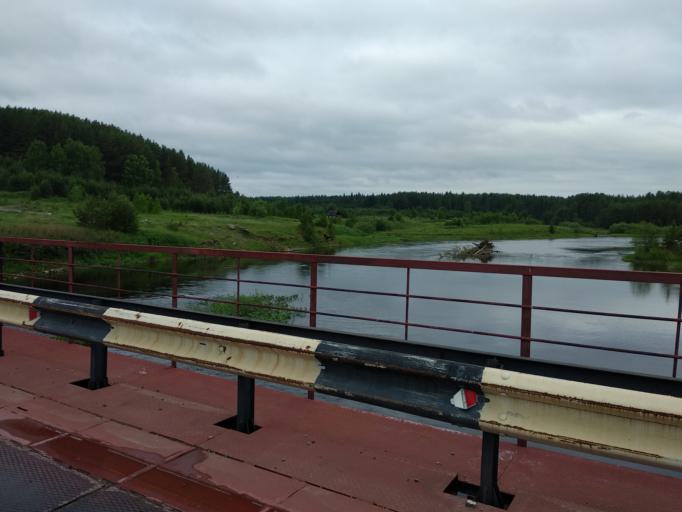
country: RU
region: Sverdlovsk
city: Karpinsk
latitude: 59.3907
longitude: 59.9480
